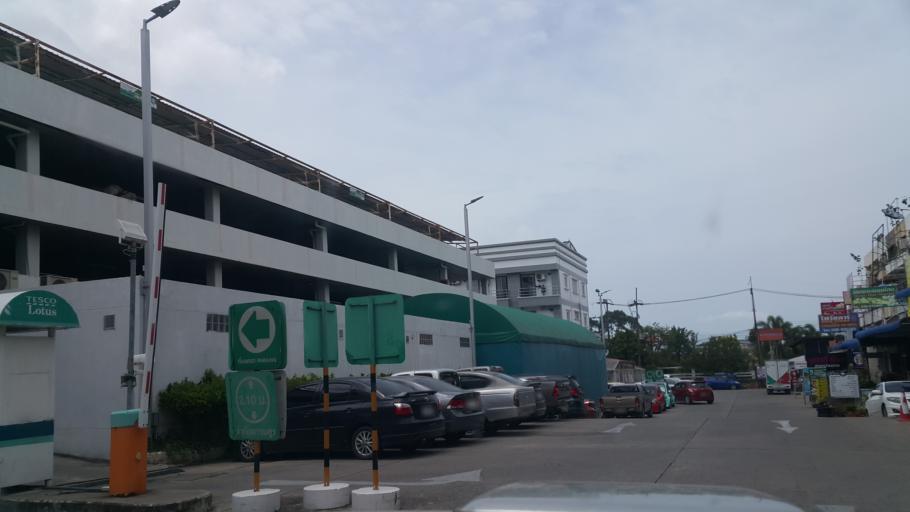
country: TH
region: Rayong
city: Ban Chang
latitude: 12.7197
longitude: 101.0476
